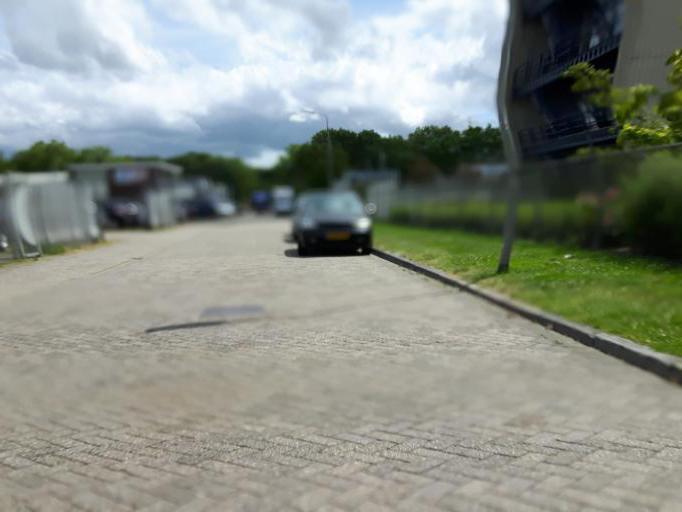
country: NL
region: Zeeland
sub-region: Gemeente Goes
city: Goes
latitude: 51.4970
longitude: 3.8848
